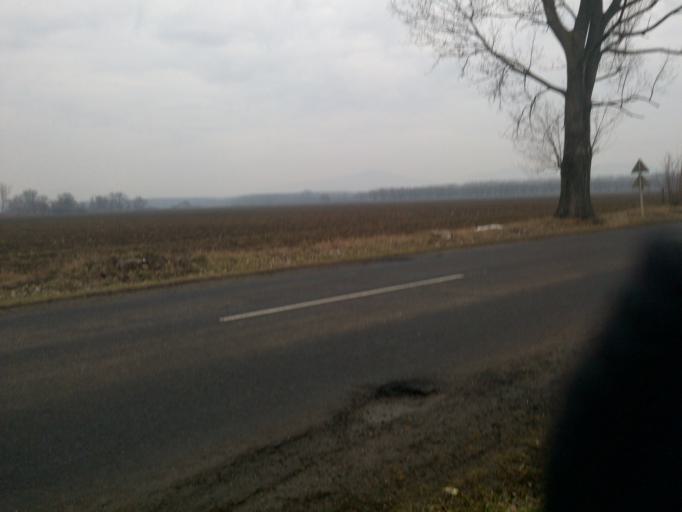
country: HU
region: Borsod-Abauj-Zemplen
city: Encs
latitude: 48.3295
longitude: 21.1394
